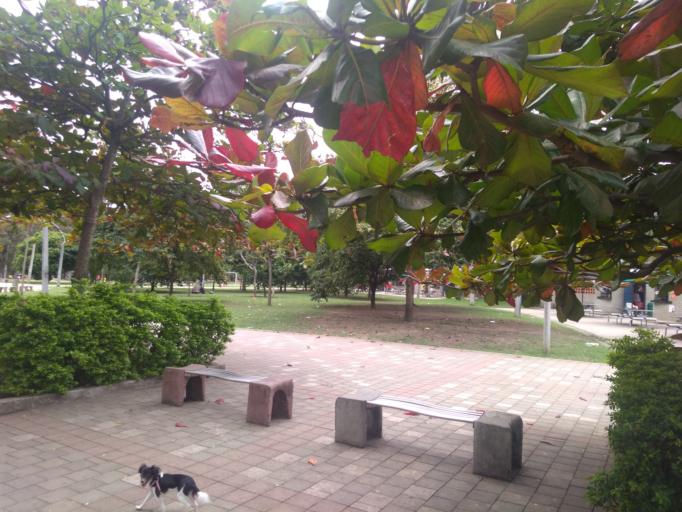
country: CO
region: Antioquia
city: Bello
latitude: 6.3355
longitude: -75.5476
